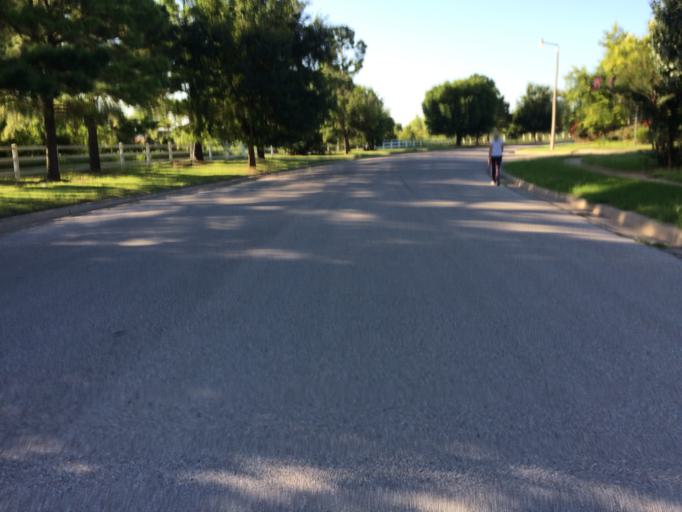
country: US
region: Oklahoma
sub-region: Cleveland County
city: Norman
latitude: 35.2109
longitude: -97.4878
